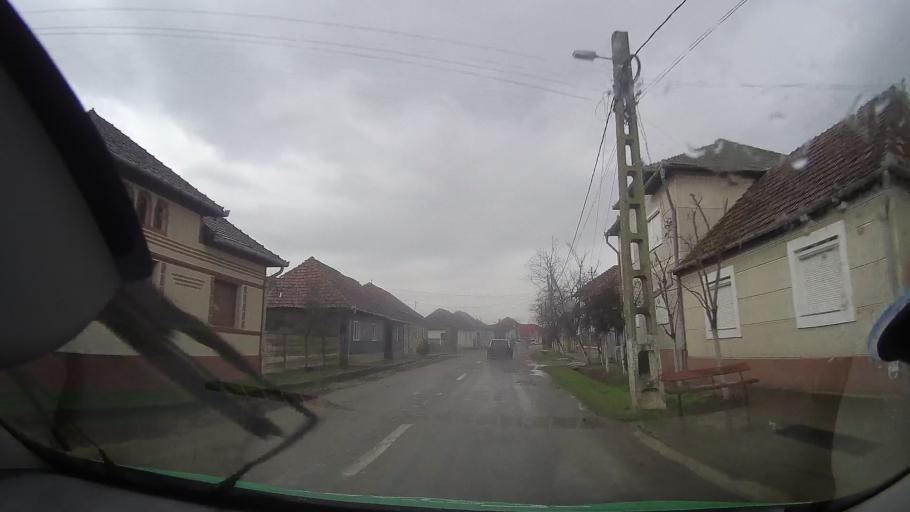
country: RO
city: Capalna
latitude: 46.7086
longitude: 22.0833
